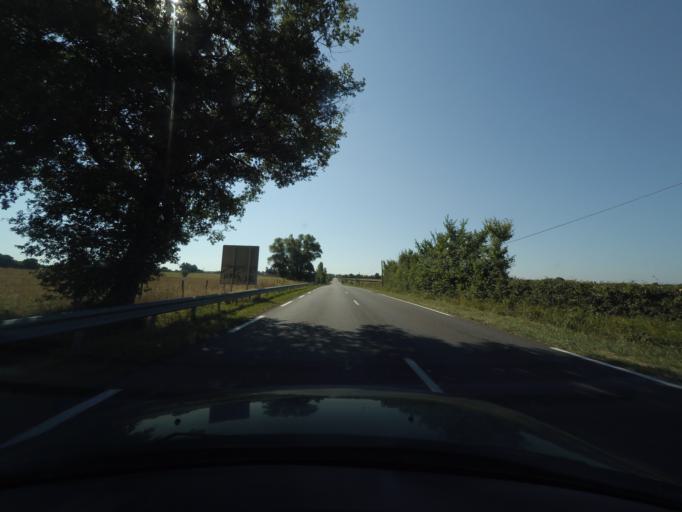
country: FR
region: Poitou-Charentes
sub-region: Departement de la Vienne
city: Lussac-les-Chateaux
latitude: 46.3740
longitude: 0.7595
